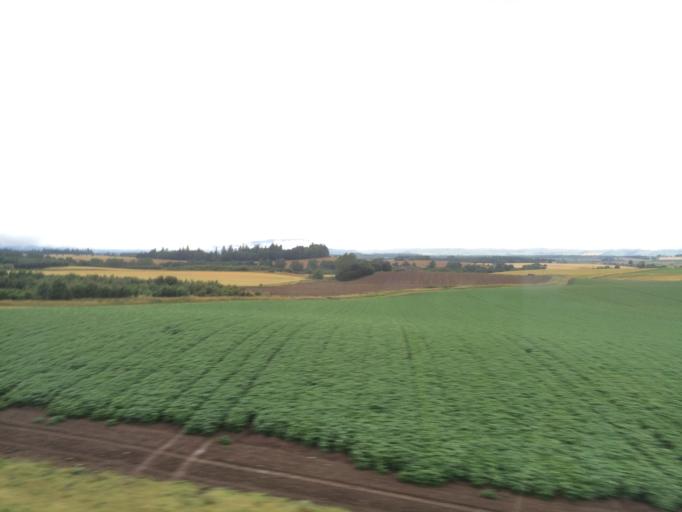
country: GB
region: Scotland
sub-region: Perth and Kinross
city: Auchterarder
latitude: 56.3043
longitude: -3.6535
